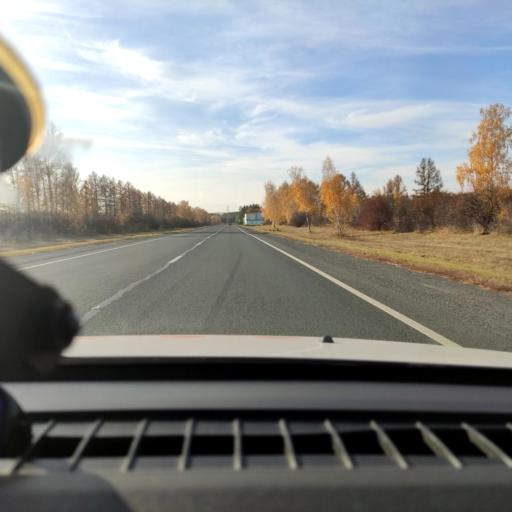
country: RU
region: Samara
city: Volzhskiy
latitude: 53.4588
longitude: 50.1269
